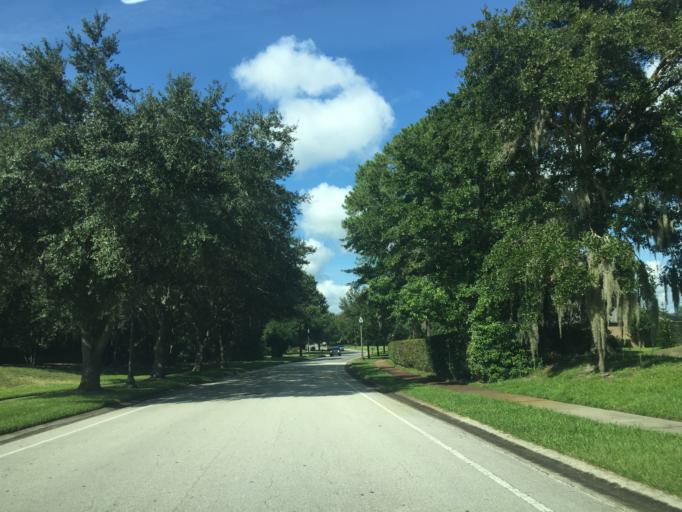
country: US
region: Florida
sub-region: Seminole County
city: Oviedo
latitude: 28.6670
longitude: -81.2409
